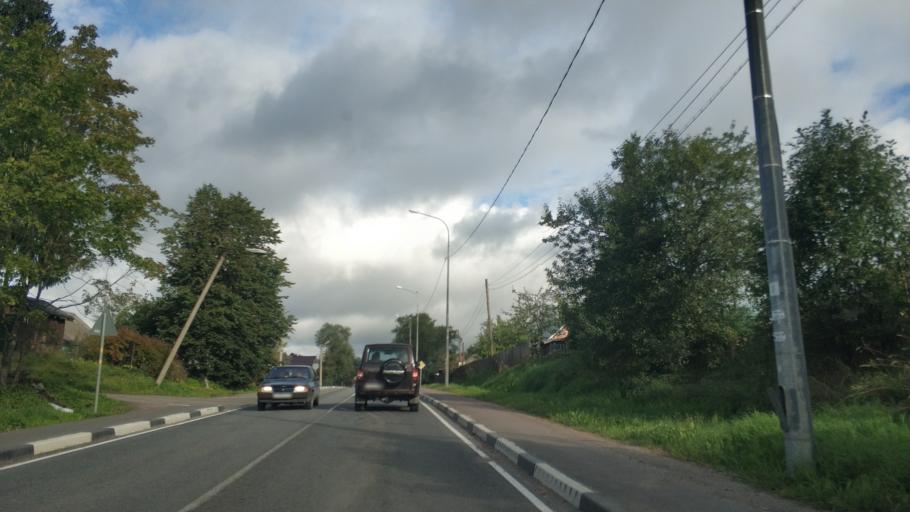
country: RU
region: Republic of Karelia
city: Khelyulya
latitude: 61.7491
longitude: 30.6642
